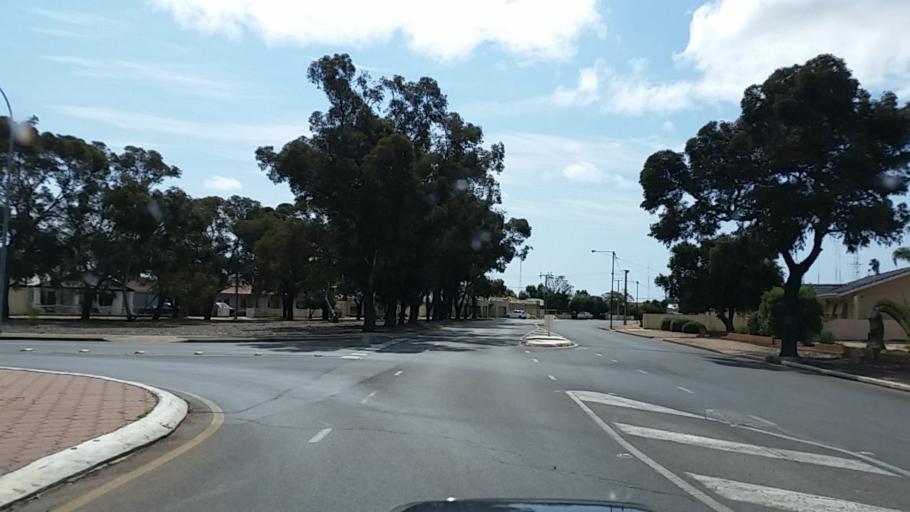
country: AU
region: South Australia
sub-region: Port Pirie City and Dists
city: Port Pirie
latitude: -33.2040
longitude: 138.0109
